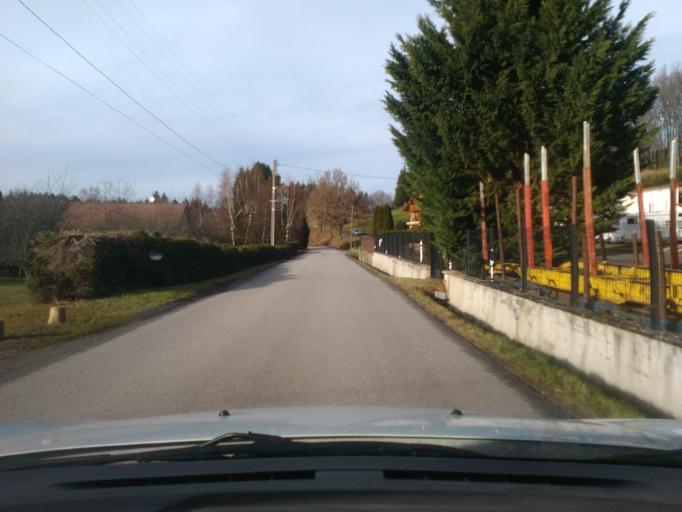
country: FR
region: Lorraine
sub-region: Departement des Vosges
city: Fraize
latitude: 48.1768
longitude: 6.9769
